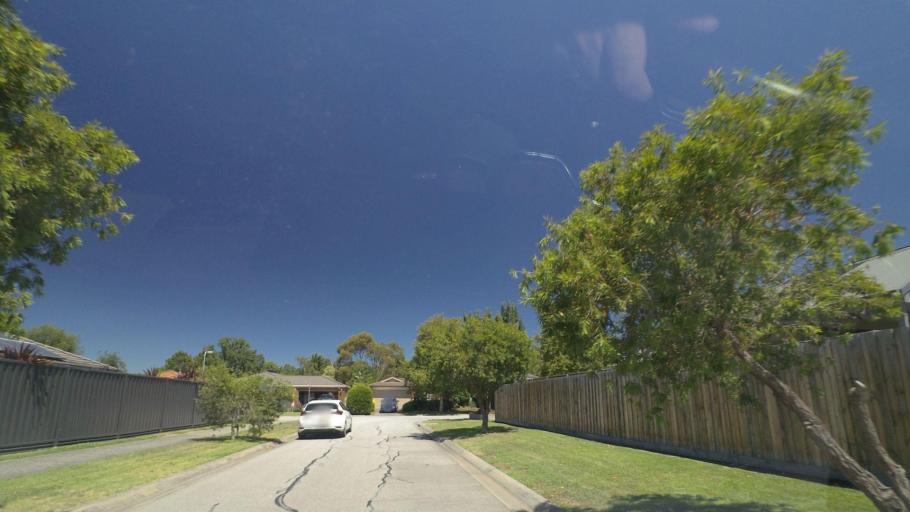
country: AU
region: Victoria
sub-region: Yarra Ranges
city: Lilydale
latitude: -37.7416
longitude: 145.3492
